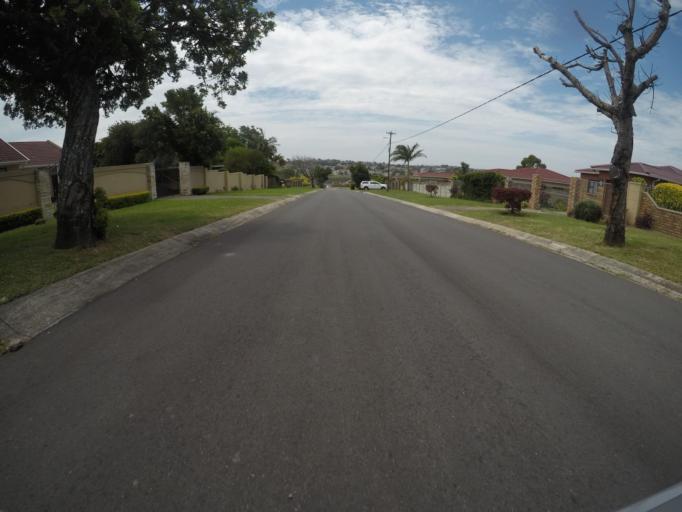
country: ZA
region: Eastern Cape
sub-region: Buffalo City Metropolitan Municipality
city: East London
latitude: -32.9833
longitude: 27.8655
